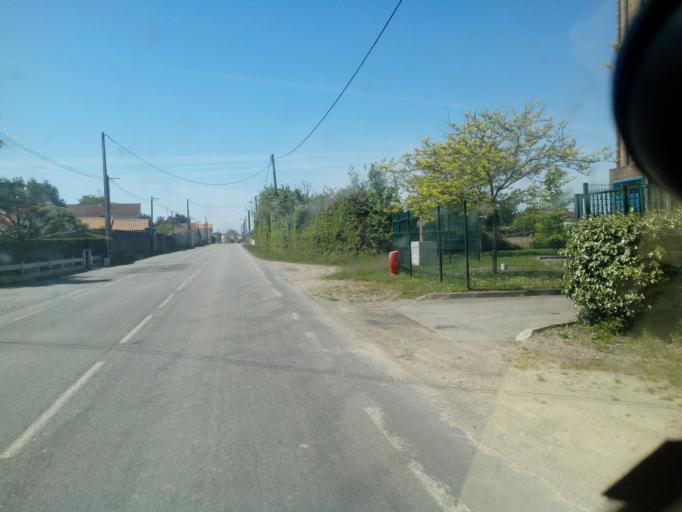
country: FR
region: Pays de la Loire
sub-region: Departement de la Loire-Atlantique
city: Pornic
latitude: 47.1083
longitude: -2.0827
